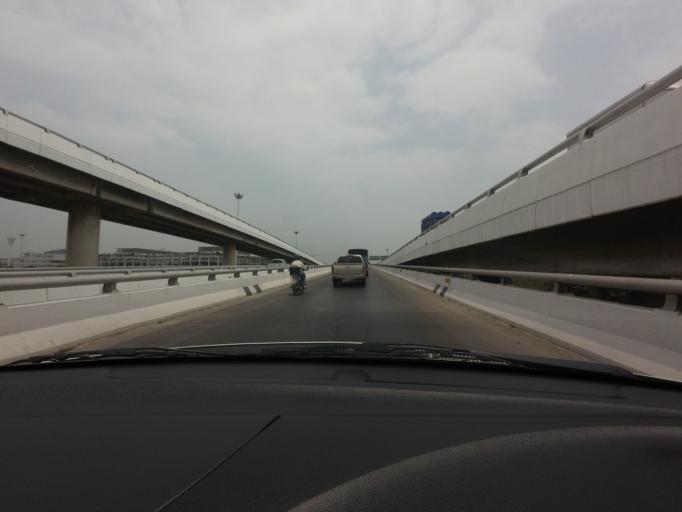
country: TH
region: Bangkok
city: Thawi Watthana
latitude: 13.7866
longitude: 100.3278
